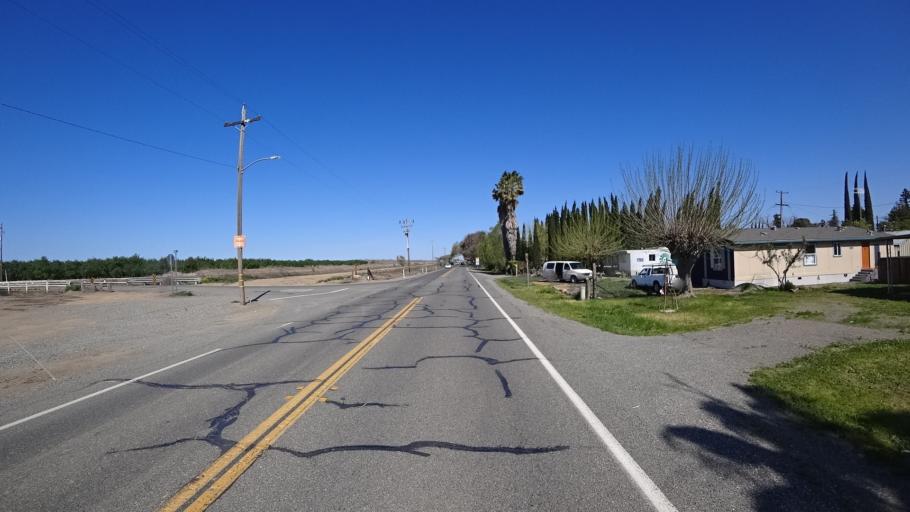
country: US
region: California
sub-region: Glenn County
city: Hamilton City
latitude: 39.7374
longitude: -122.0159
